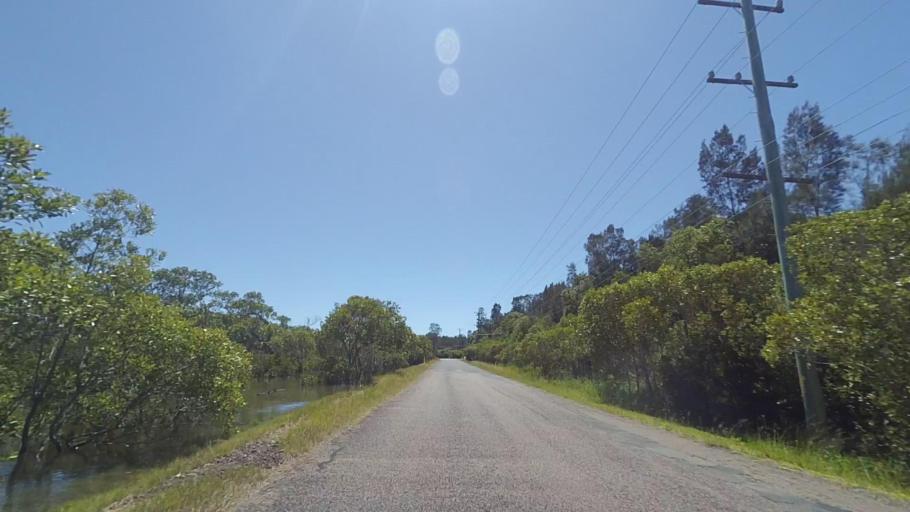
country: AU
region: New South Wales
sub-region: Port Stephens Shire
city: Medowie
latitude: -32.7783
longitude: 151.9647
